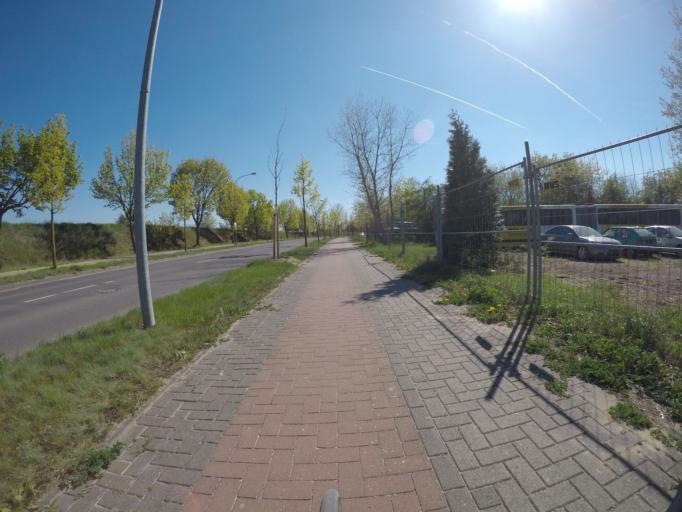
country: DE
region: Brandenburg
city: Strausberg
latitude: 52.5797
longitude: 13.9082
